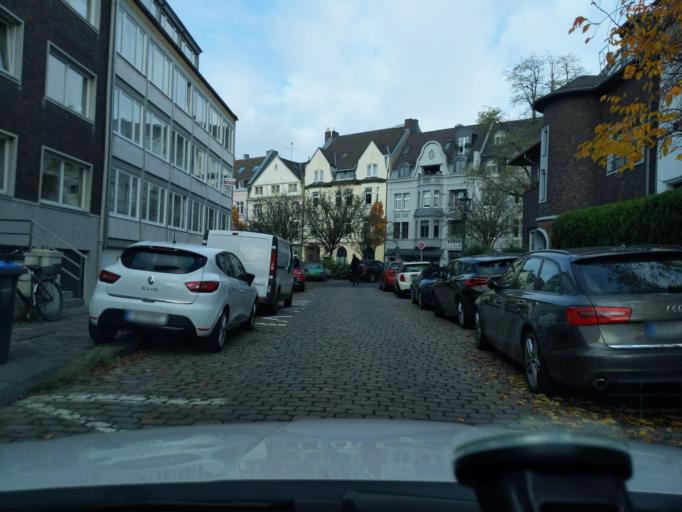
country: DE
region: North Rhine-Westphalia
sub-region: Regierungsbezirk Dusseldorf
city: Dusseldorf
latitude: 51.2312
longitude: 6.7438
